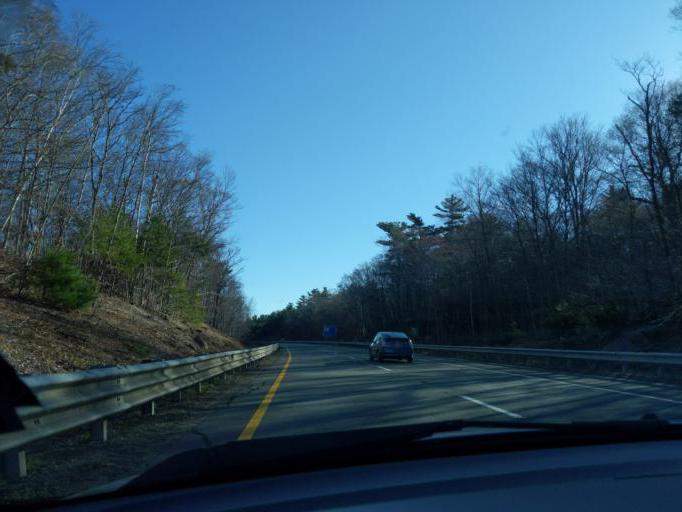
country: US
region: Massachusetts
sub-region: Essex County
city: Essex
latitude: 42.6058
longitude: -70.7393
